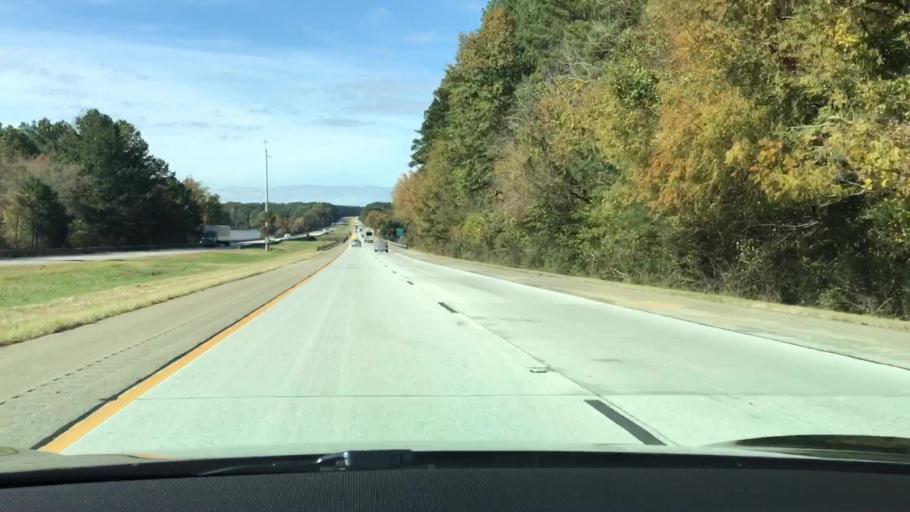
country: US
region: Georgia
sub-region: Greene County
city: Greensboro
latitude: 33.5346
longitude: -83.2664
